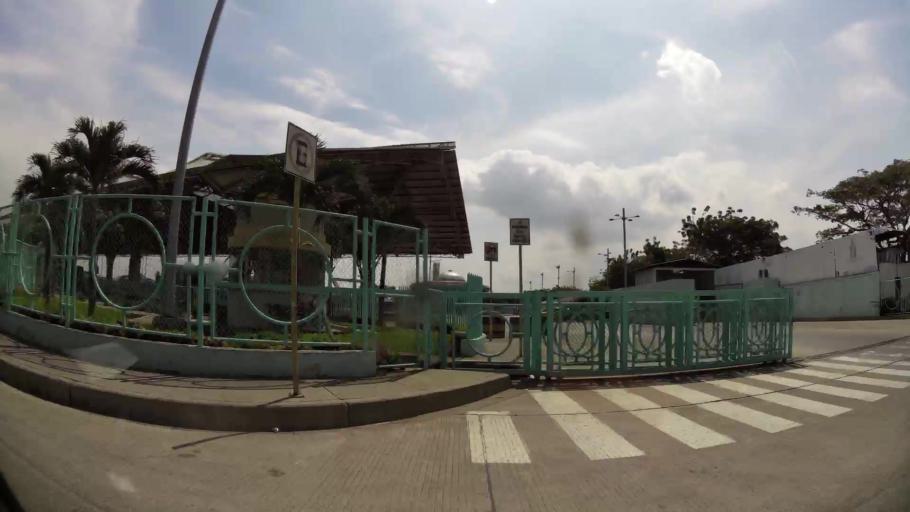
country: EC
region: Guayas
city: Guayaquil
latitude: -2.2622
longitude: -79.8730
